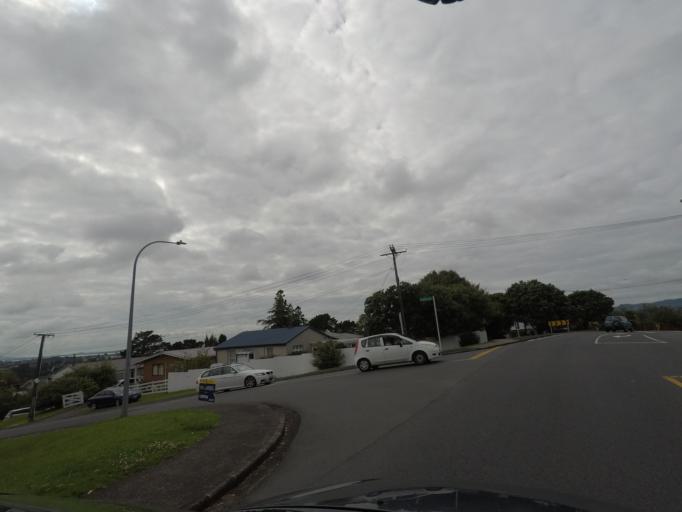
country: NZ
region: Auckland
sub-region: Auckland
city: Rosebank
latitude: -36.8541
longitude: 174.6119
